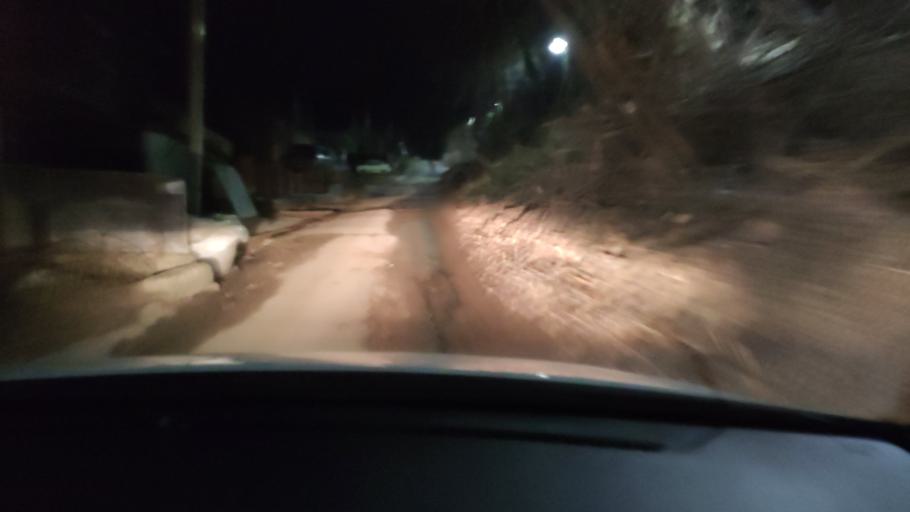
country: RU
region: Tatarstan
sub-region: Gorod Kazan'
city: Kazan
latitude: 55.8437
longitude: 49.2092
